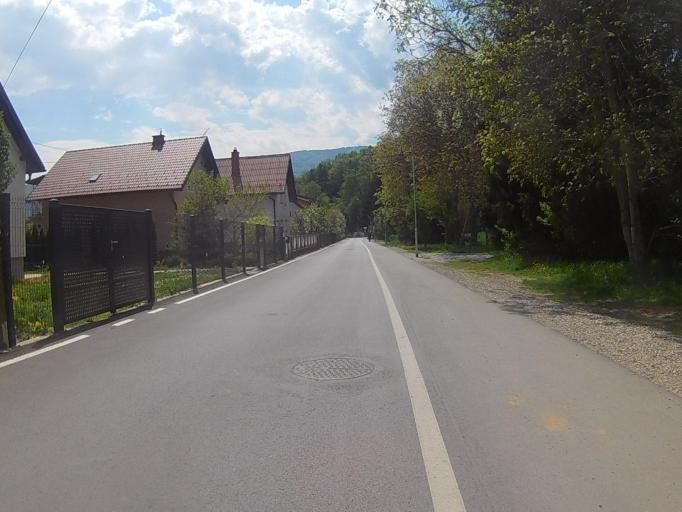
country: SI
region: Maribor
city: Pekre
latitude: 46.5504
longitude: 15.6119
